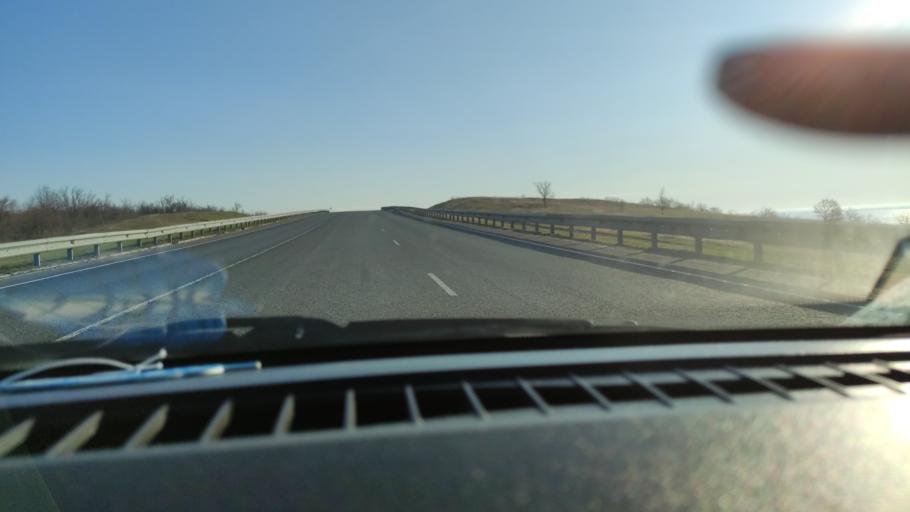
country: RU
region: Saratov
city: Alekseyevka
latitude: 52.2063
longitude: 47.8734
